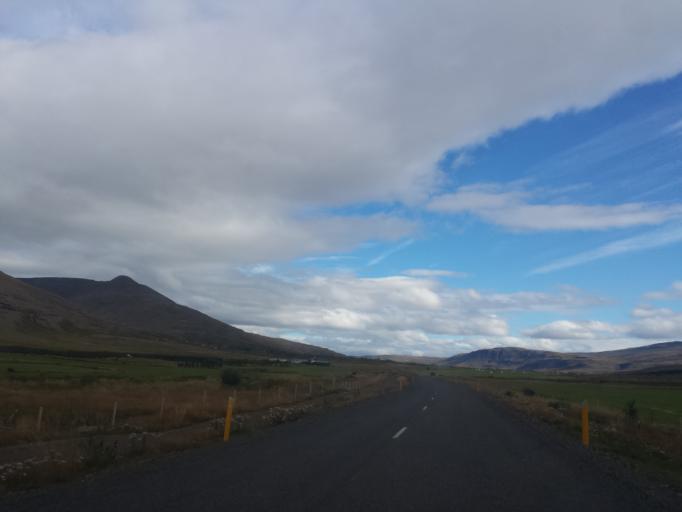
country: IS
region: West
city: Borgarnes
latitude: 64.4282
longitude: -21.6840
